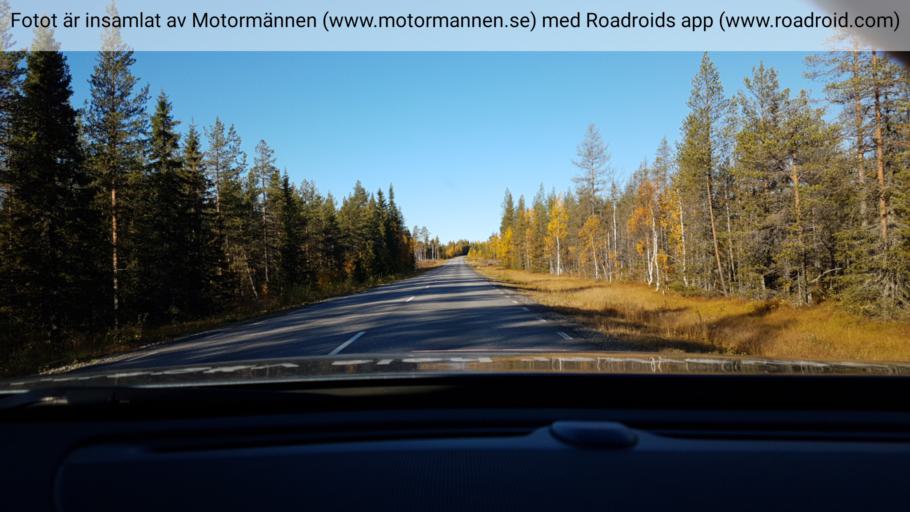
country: SE
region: Vaesterbotten
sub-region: Skelleftea Kommun
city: Storvik
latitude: 65.3372
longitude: 20.5500
